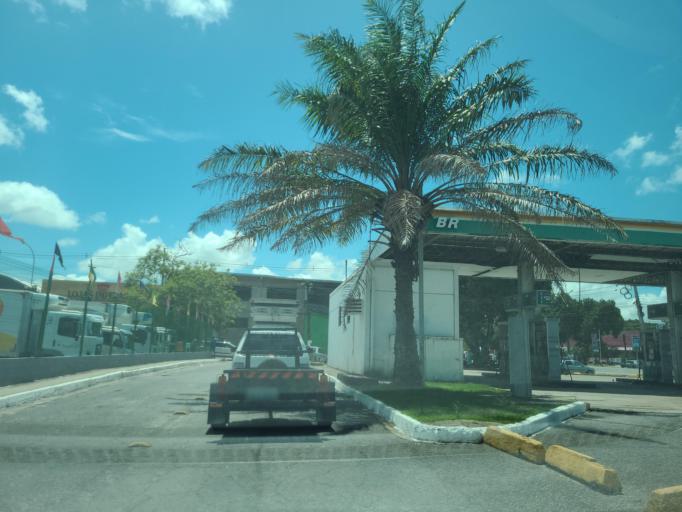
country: BR
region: Alagoas
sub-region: Maceio
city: Maceio
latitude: -9.5961
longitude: -35.7519
